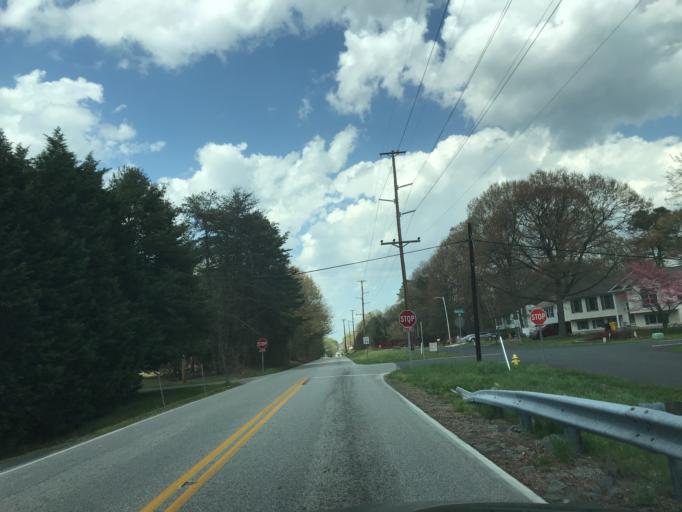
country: US
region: Maryland
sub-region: Anne Arundel County
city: Severn
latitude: 39.1418
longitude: -76.6711
